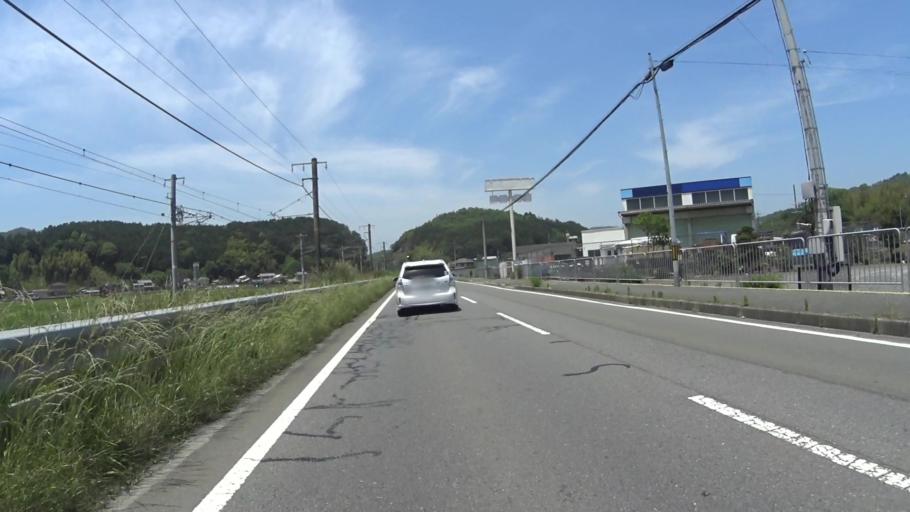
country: JP
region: Kyoto
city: Kameoka
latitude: 35.0779
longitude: 135.5200
